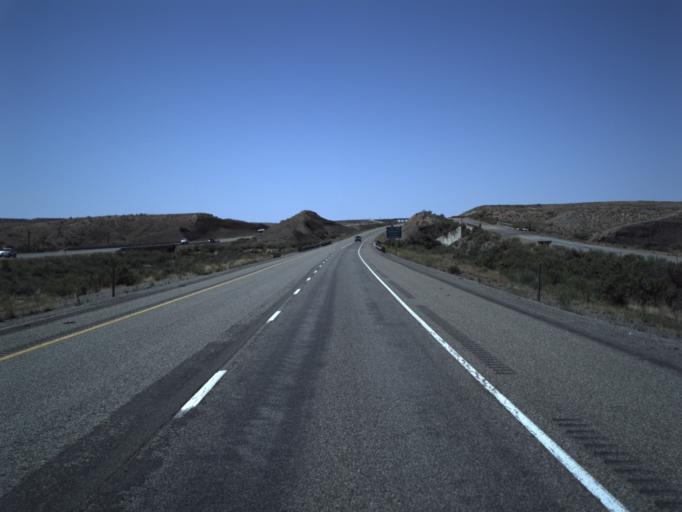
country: US
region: Colorado
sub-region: Mesa County
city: Loma
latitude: 39.1246
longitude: -109.1691
